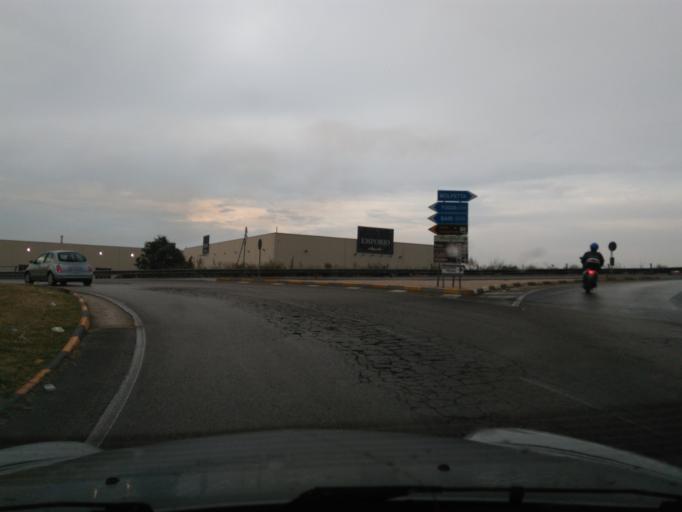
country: IT
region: Apulia
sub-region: Provincia di Bari
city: Molfetta
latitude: 41.2078
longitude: 16.5625
